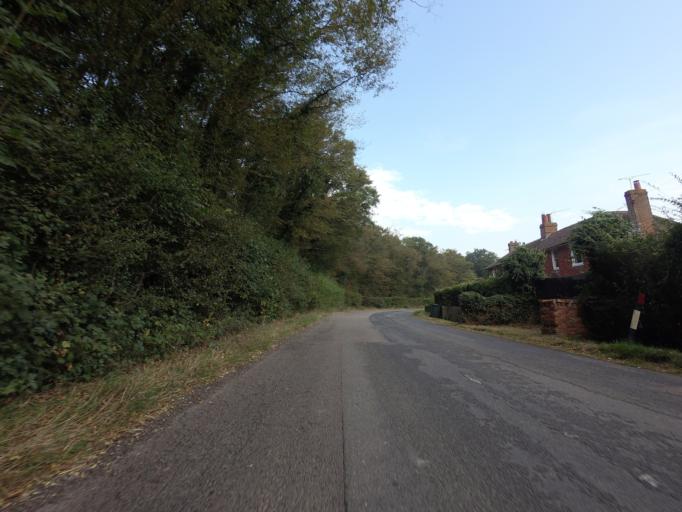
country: GB
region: England
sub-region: Kent
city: Ashford
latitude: 51.1060
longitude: 0.7938
